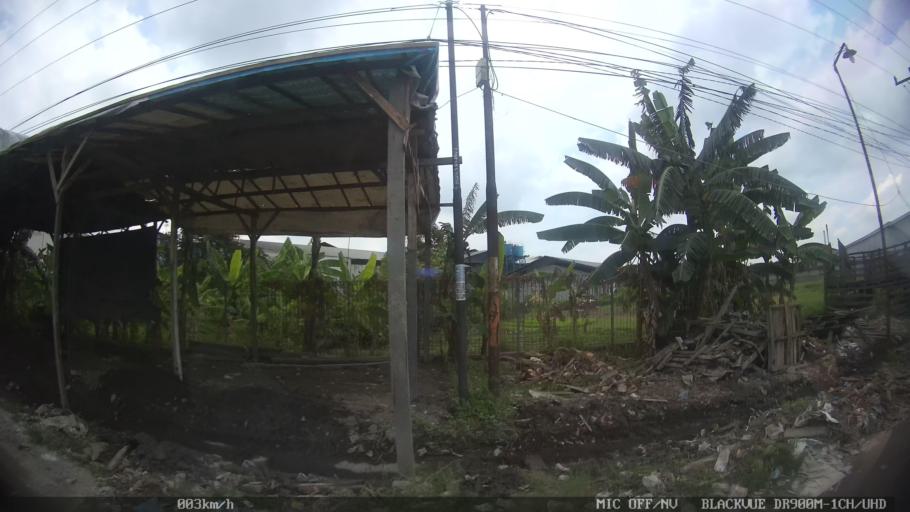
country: ID
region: North Sumatra
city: Labuhan Deli
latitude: 3.6754
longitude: 98.6740
